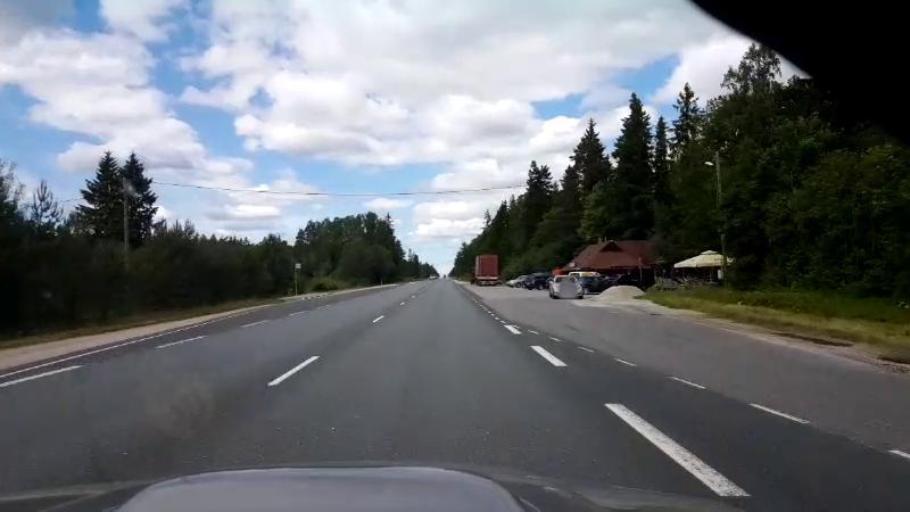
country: EE
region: Raplamaa
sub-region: Maerjamaa vald
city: Marjamaa
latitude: 58.9933
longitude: 24.4656
